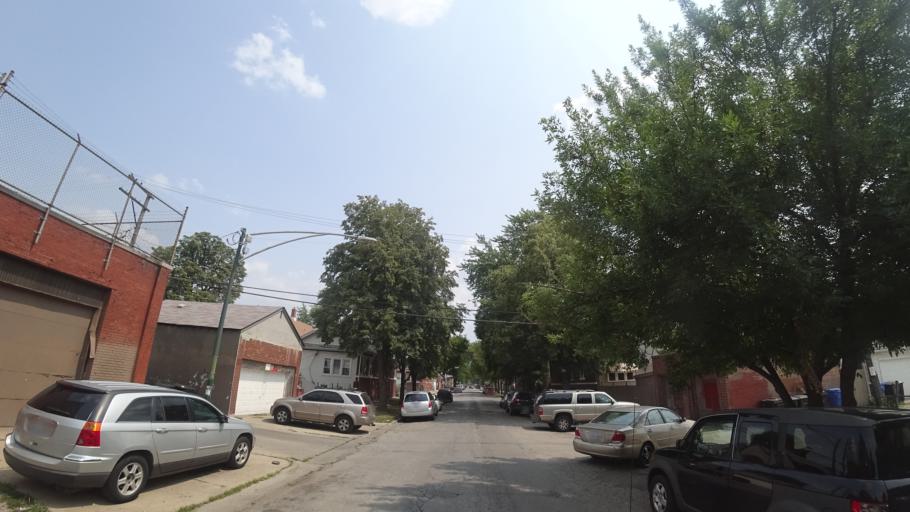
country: US
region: Illinois
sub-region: Cook County
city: Cicero
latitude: 41.8423
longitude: -87.7314
